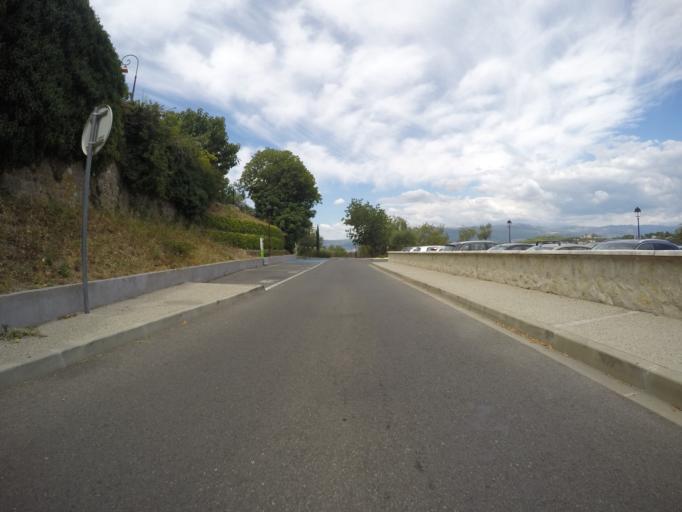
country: FR
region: Provence-Alpes-Cote d'Azur
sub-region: Departement des Alpes-Maritimes
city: Mougins
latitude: 43.6013
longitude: 6.9959
